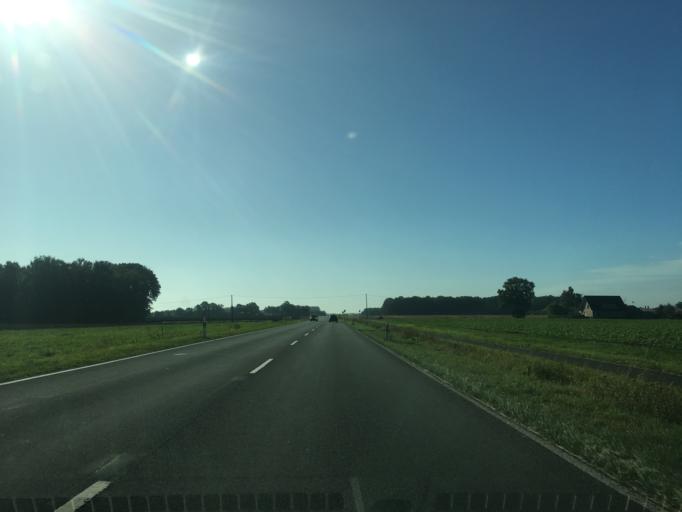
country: DE
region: North Rhine-Westphalia
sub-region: Regierungsbezirk Munster
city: Senden
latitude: 51.8265
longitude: 7.4923
